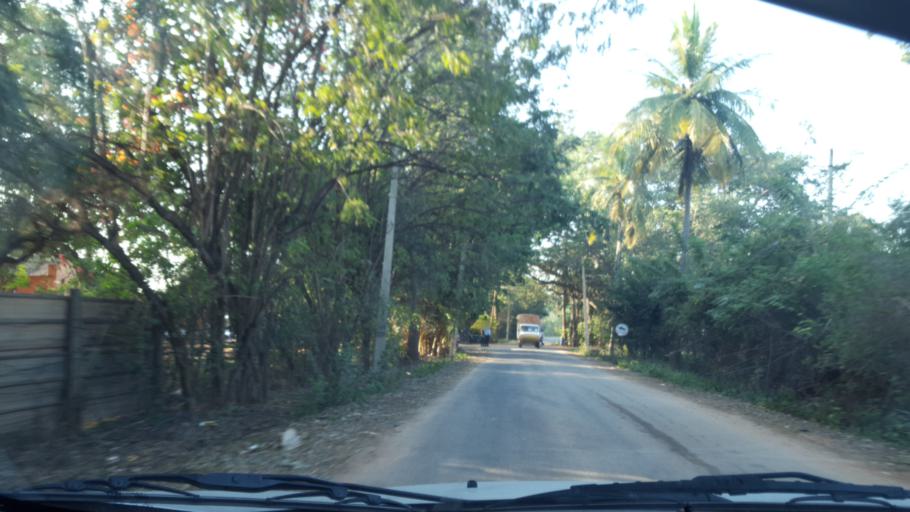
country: IN
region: Karnataka
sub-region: Bangalore Urban
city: Yelahanka
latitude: 13.1739
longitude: 77.5955
